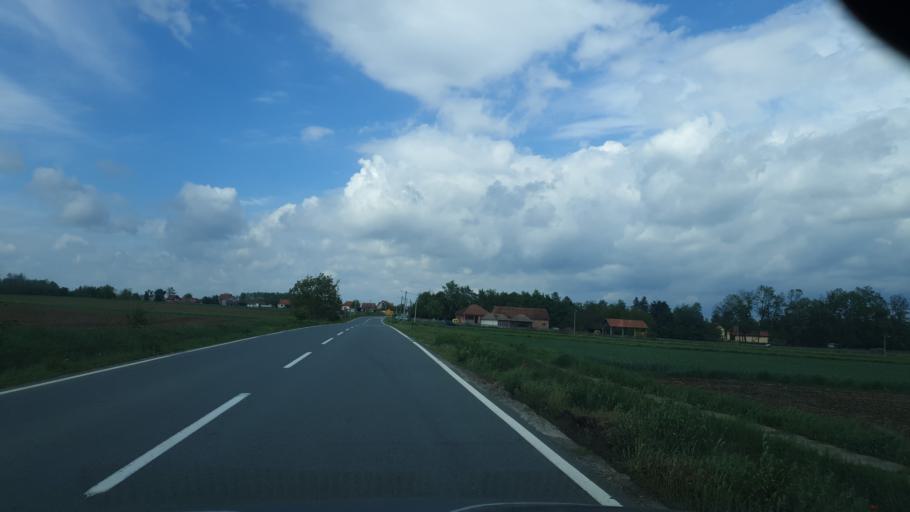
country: RS
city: Stubline
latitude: 44.5372
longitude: 20.1227
